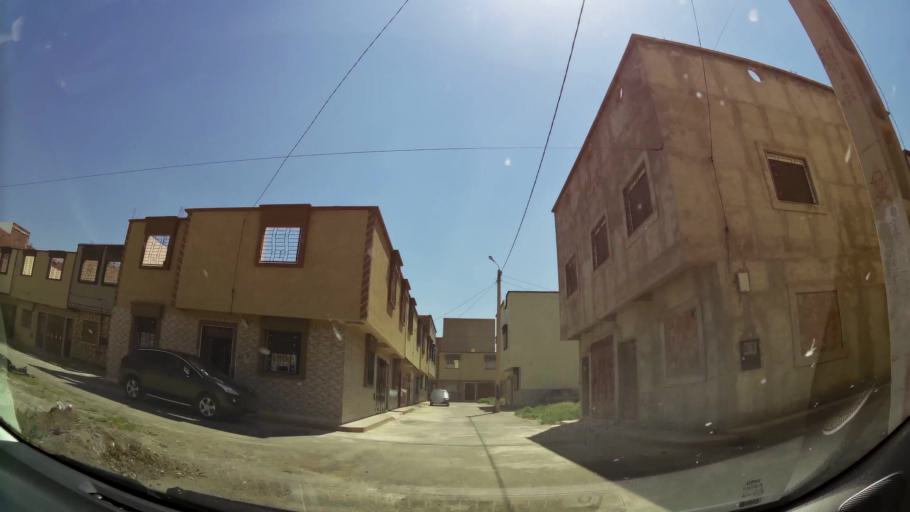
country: MA
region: Oriental
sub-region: Oujda-Angad
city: Oujda
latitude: 34.6916
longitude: -1.9385
